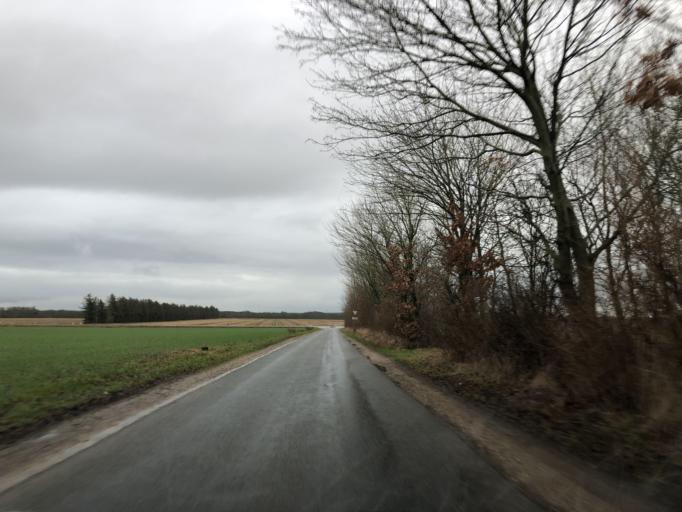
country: DK
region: Central Jutland
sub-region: Holstebro Kommune
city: Holstebro
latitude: 56.3727
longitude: 8.7289
